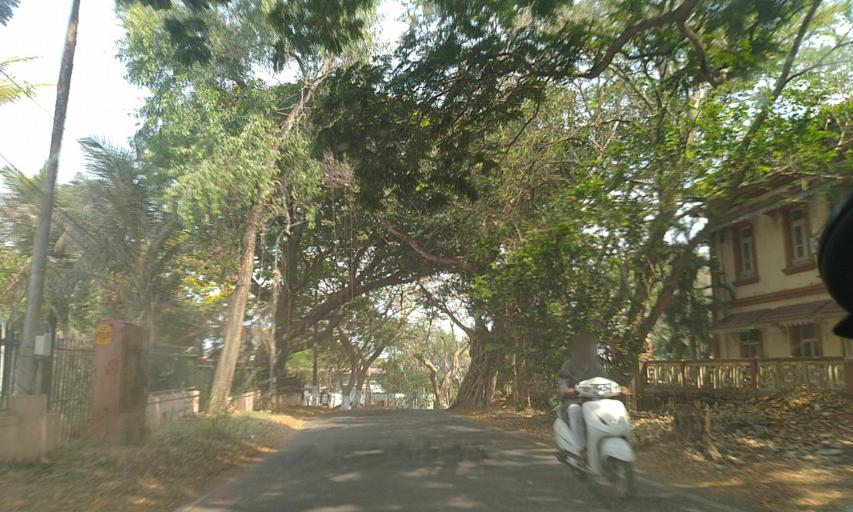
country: IN
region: Goa
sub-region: North Goa
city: Panaji
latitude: 15.4921
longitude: 73.8266
